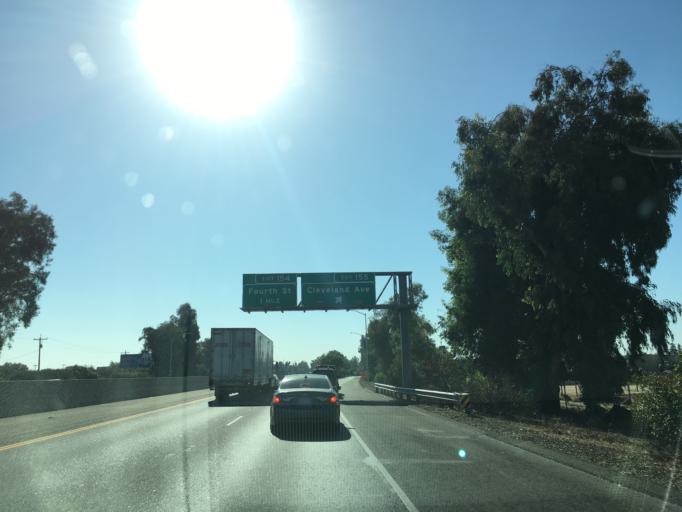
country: US
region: California
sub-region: Madera County
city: Madera
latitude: 36.9774
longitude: -120.0799
